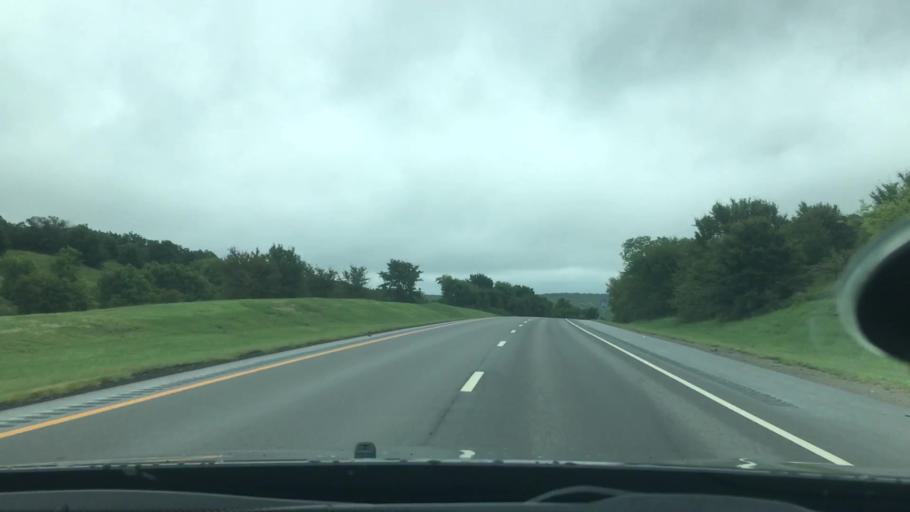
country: US
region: Oklahoma
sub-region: Okmulgee County
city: Henryetta
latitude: 35.4366
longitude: -95.8327
